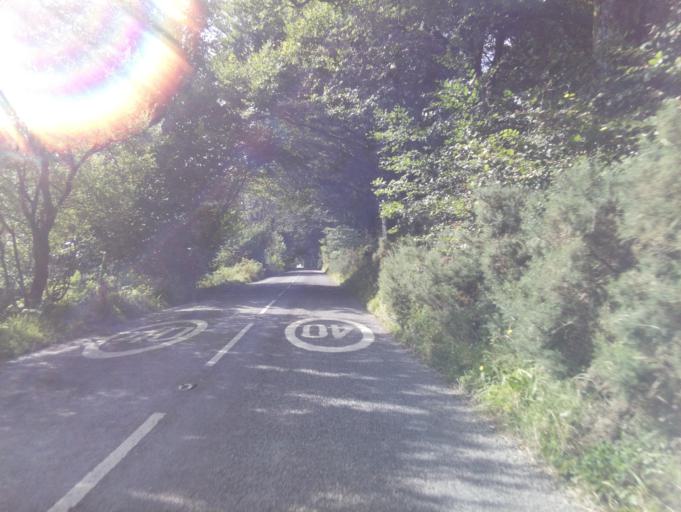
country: GB
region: England
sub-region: Devon
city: Buckfastleigh
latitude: 50.5454
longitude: -3.8878
